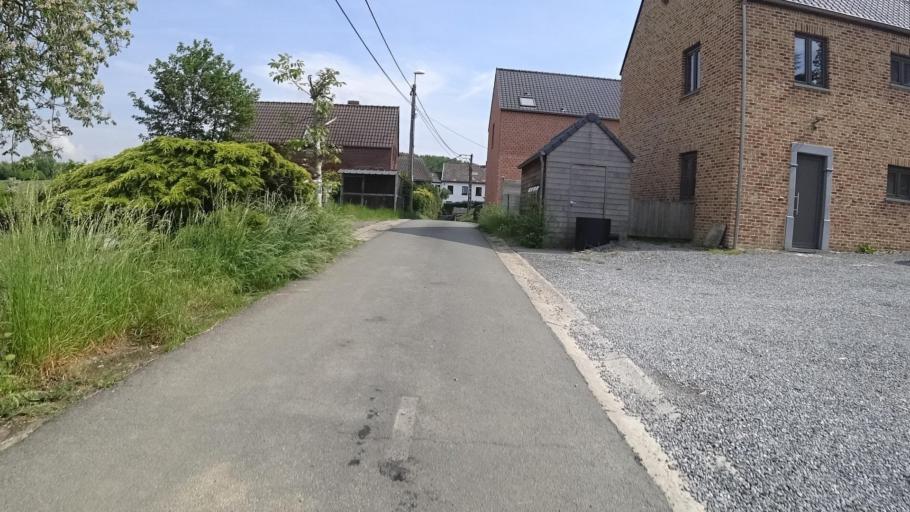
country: BE
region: Wallonia
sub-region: Province du Brabant Wallon
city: Louvain-la-Neuve
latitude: 50.6735
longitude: 4.6482
